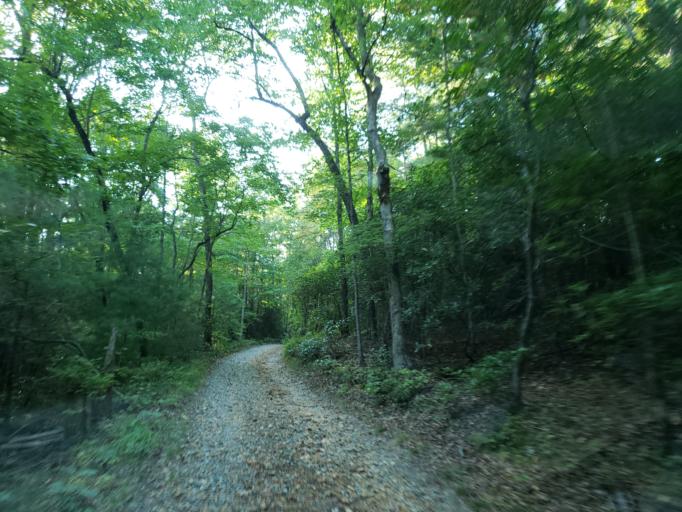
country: US
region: Georgia
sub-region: Fannin County
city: Blue Ridge
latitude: 34.7007
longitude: -84.2641
